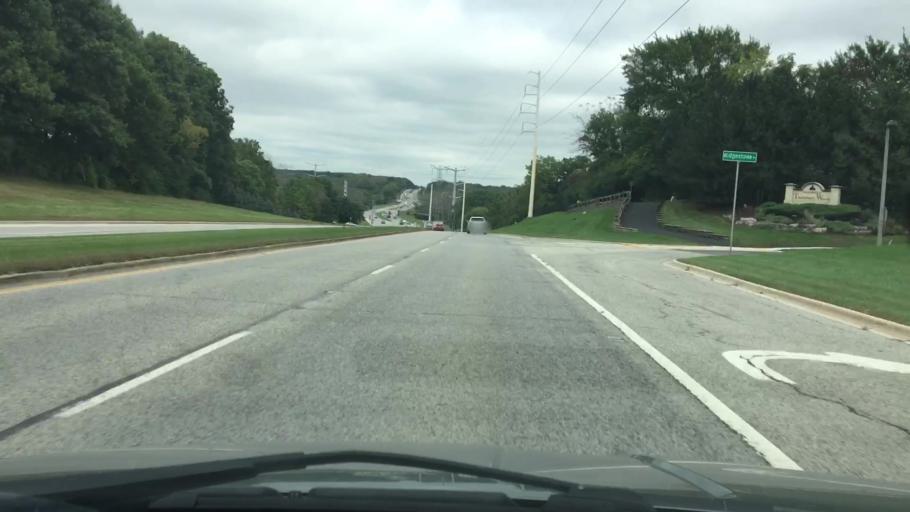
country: US
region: Illinois
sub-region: DuPage County
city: Woodridge
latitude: 41.7492
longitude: -88.0790
